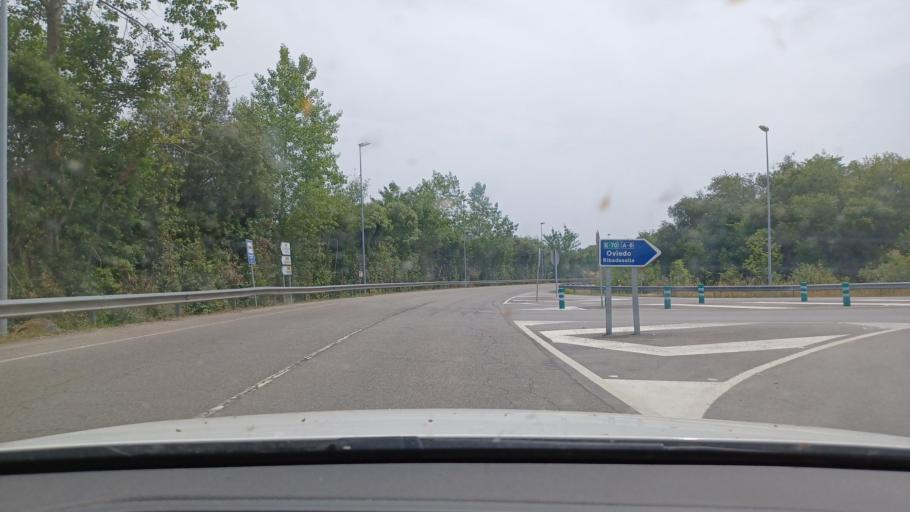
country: ES
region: Asturias
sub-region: Province of Asturias
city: Ribadesella
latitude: 43.4404
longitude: -4.9614
